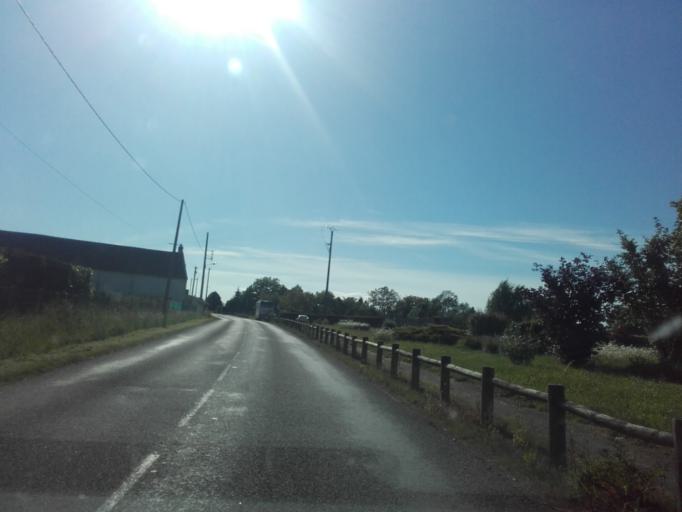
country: FR
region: Bourgogne
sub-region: Departement de Saone-et-Loire
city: Chagny
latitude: 46.9130
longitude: 4.7862
